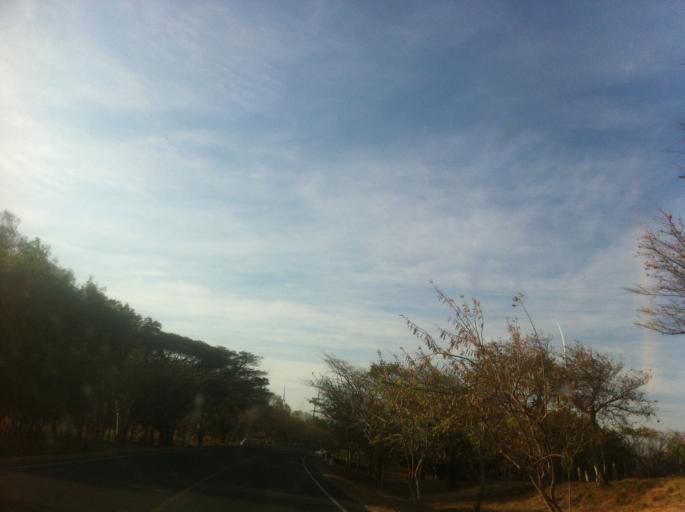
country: NI
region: Rivas
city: San Jorge
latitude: 11.3262
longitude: -85.7170
